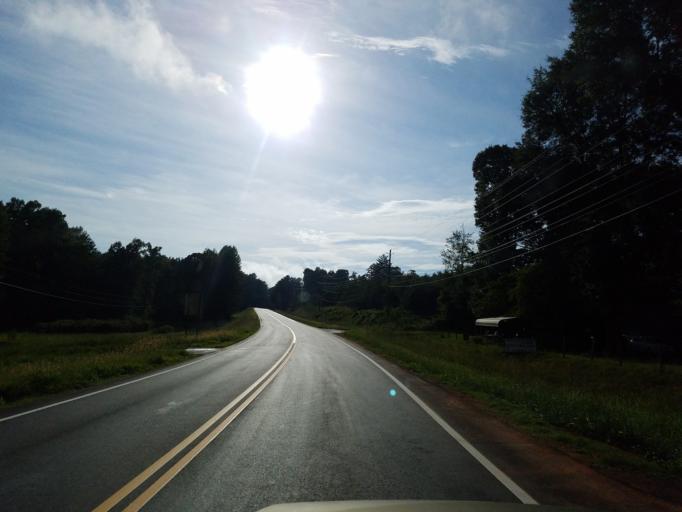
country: US
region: Georgia
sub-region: White County
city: Cleveland
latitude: 34.6131
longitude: -83.7801
